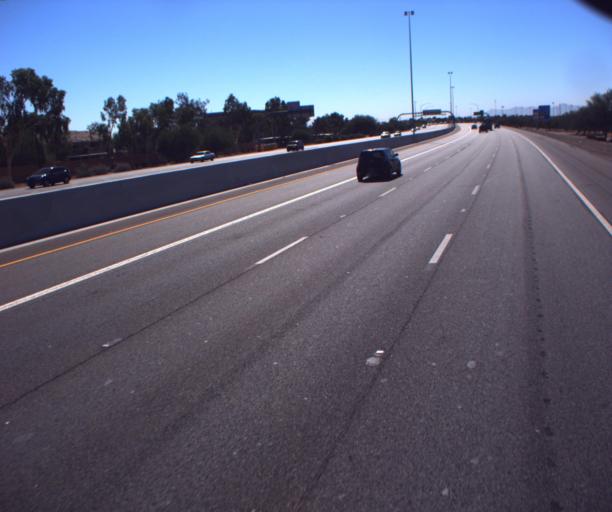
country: US
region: Arizona
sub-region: Maricopa County
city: Sun City
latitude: 33.6259
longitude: -112.2405
